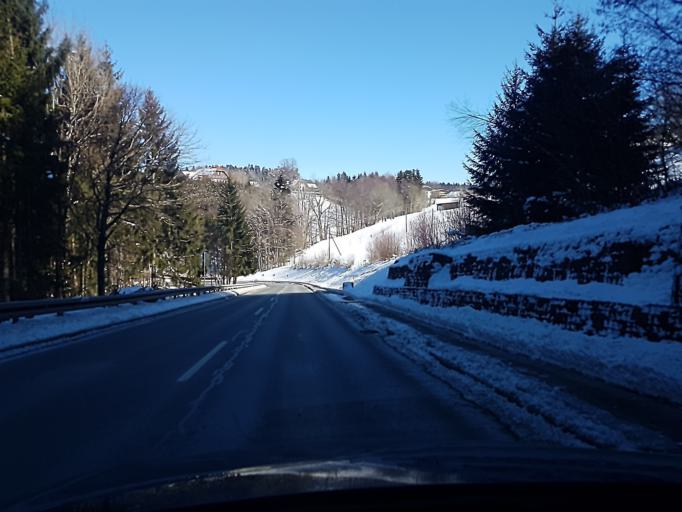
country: DE
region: Baden-Wuerttemberg
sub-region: Freiburg Region
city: Hardt
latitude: 48.1936
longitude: 8.4061
